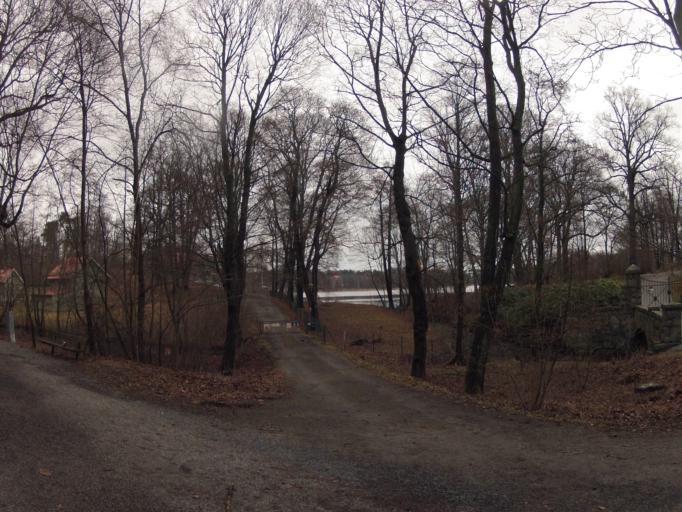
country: SE
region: Stockholm
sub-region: Norrtalje Kommun
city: Bergshamra
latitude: 59.3564
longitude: 18.0435
